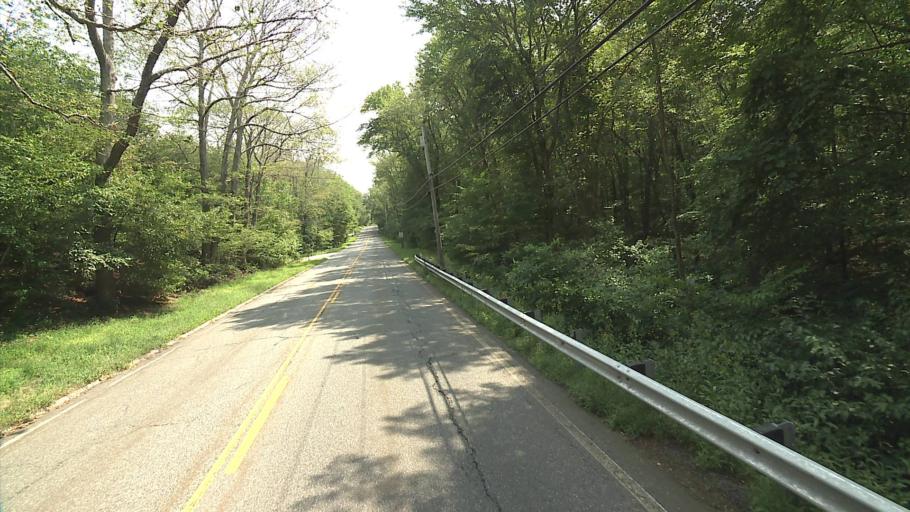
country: US
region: Connecticut
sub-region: New London County
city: Montville Center
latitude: 41.5025
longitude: -72.1852
